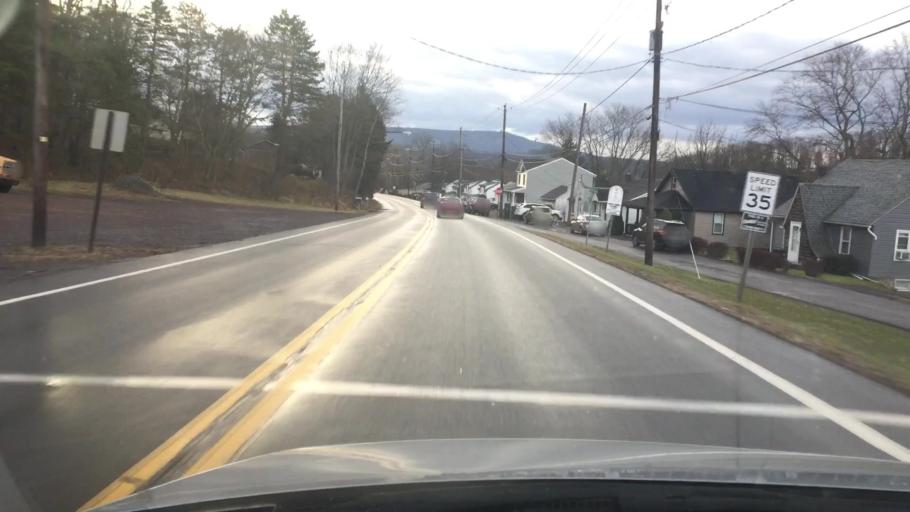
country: US
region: Pennsylvania
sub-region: Columbia County
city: Bloomsburg
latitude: 41.0124
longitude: -76.4665
